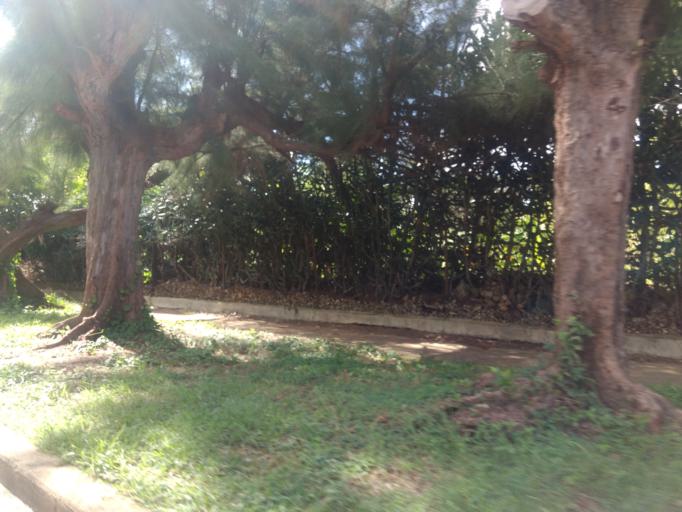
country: CU
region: La Habana
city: Cerro
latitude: 23.0788
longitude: -82.4661
